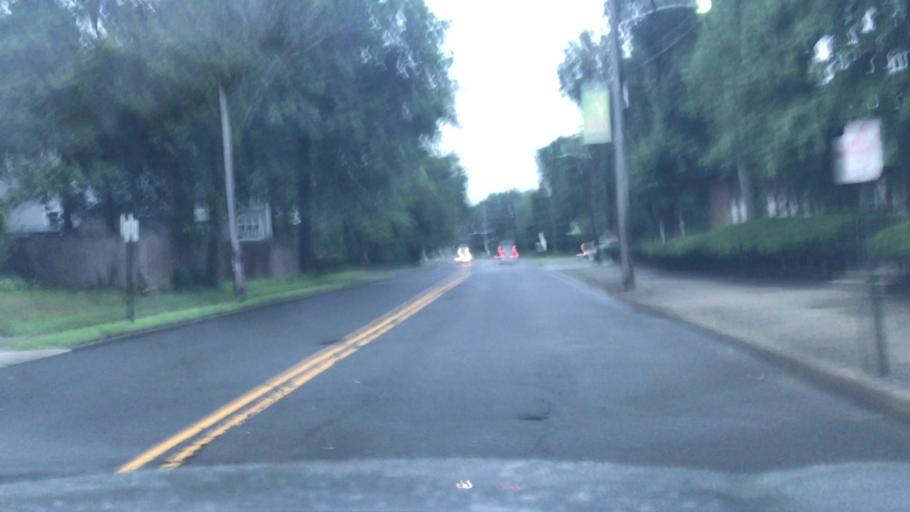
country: US
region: New Jersey
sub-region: Bergen County
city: Tenafly
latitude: 40.9201
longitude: -73.9653
